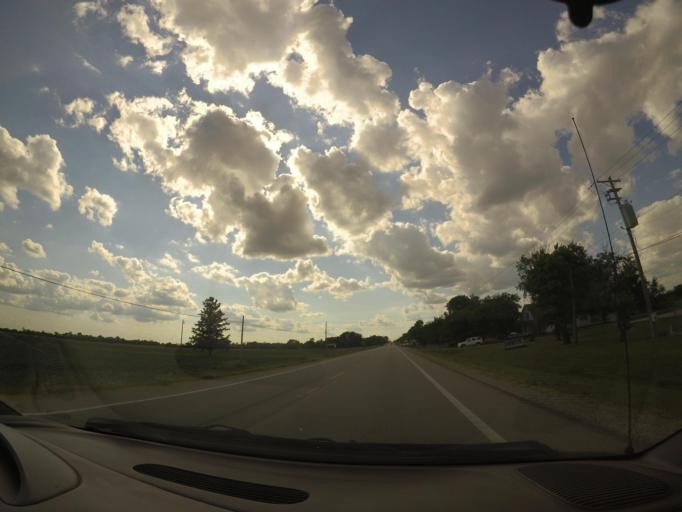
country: US
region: Ohio
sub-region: Wood County
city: Luckey
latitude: 41.5040
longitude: -83.4938
